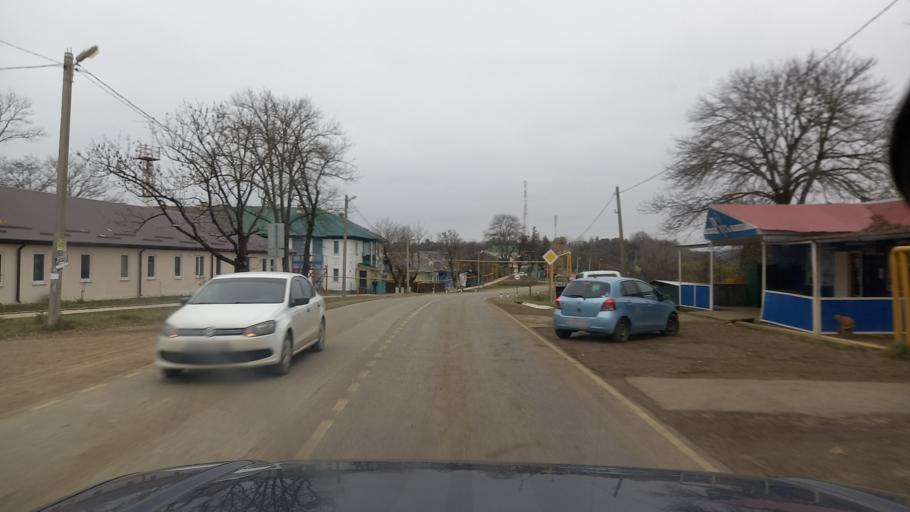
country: RU
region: Krasnodarskiy
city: Goryachiy Klyuch
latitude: 44.5179
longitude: 39.2932
